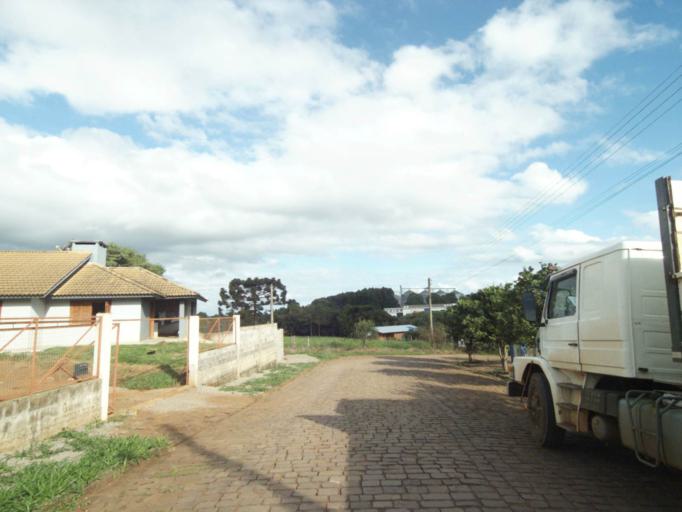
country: BR
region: Rio Grande do Sul
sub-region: Lagoa Vermelha
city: Lagoa Vermelha
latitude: -28.2070
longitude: -51.5145
